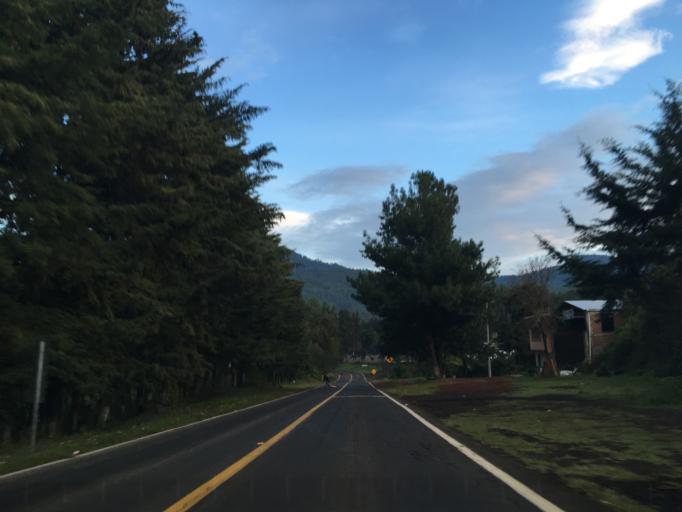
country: MX
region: Michoacan
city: Cheran
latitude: 19.6915
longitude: -101.9654
